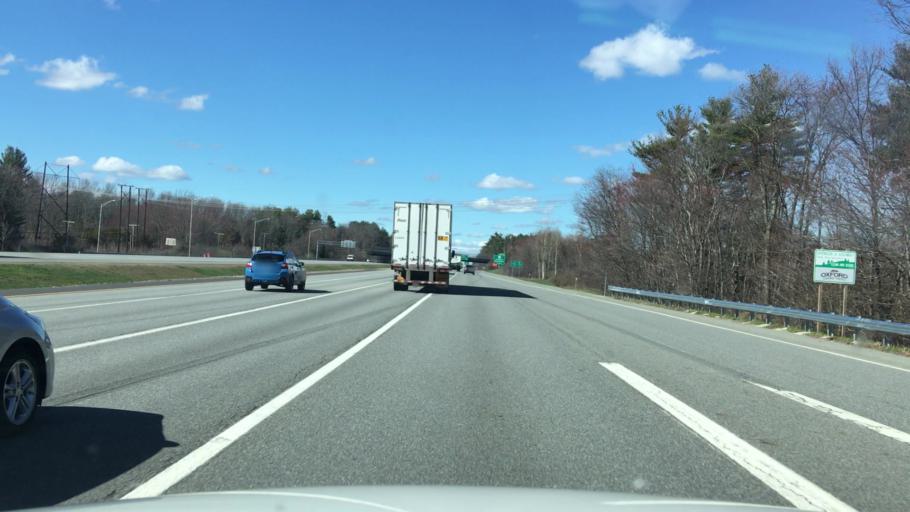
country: US
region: New Hampshire
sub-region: Rockingham County
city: Hampton Falls
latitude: 42.9374
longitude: -70.8611
